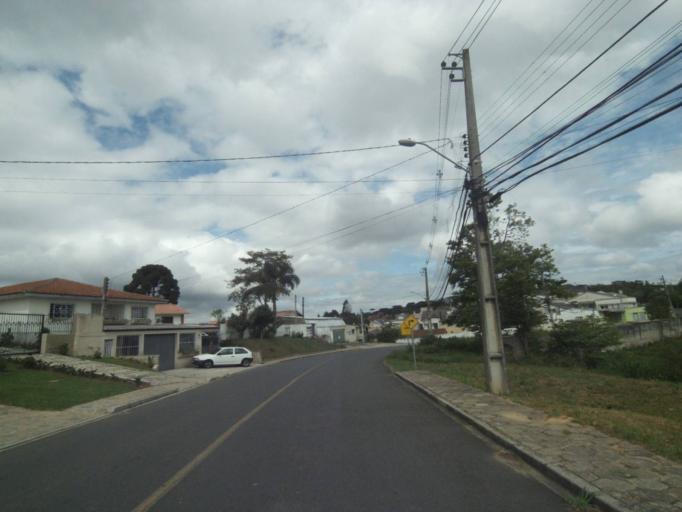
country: BR
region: Parana
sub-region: Curitiba
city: Curitiba
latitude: -25.3804
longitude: -49.2913
